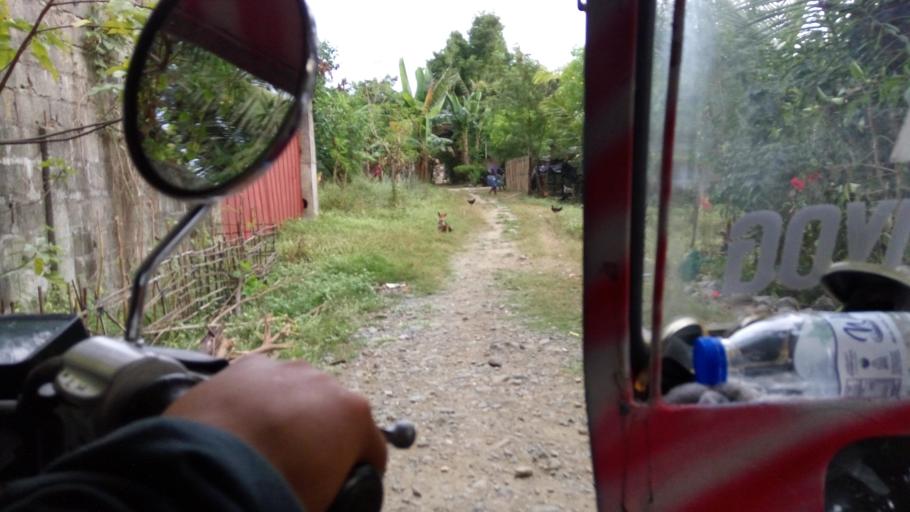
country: PH
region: Ilocos
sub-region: Province of La Union
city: Damortis
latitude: 16.2519
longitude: 120.4016
